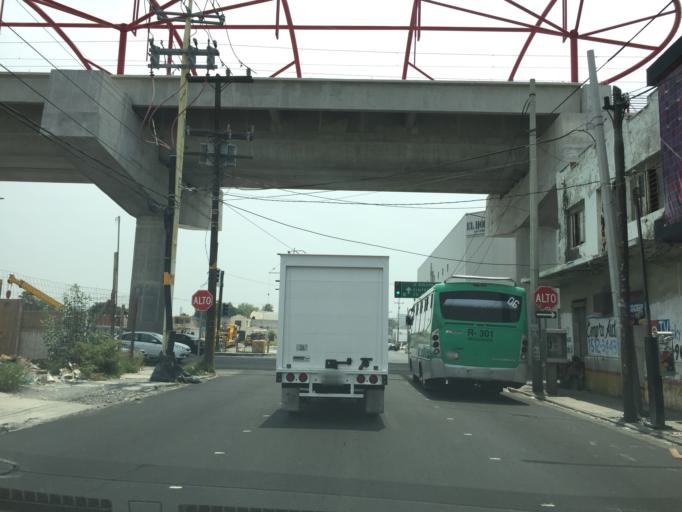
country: MX
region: Nuevo Leon
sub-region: Monterrey
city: Monterrey
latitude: 25.6779
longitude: -100.2981
